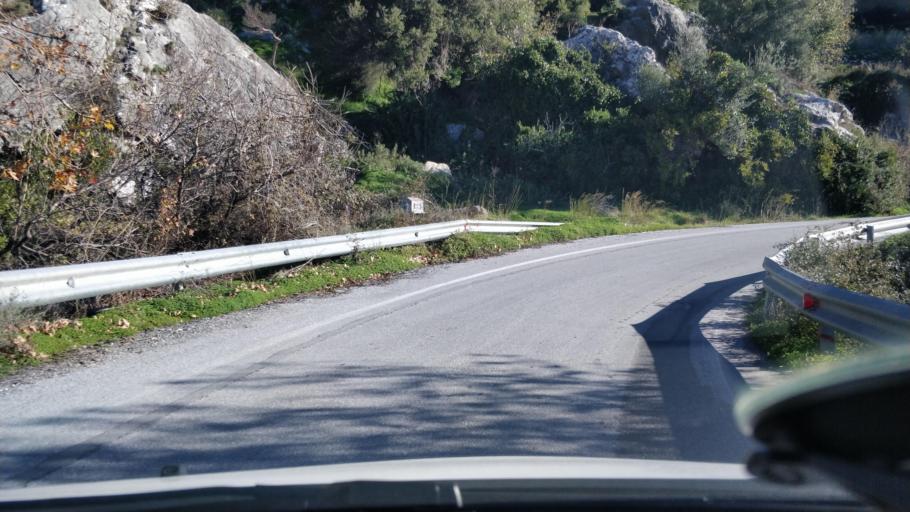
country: GR
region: Crete
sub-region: Nomos Lasithiou
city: Kritsa
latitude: 35.0803
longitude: 25.5948
